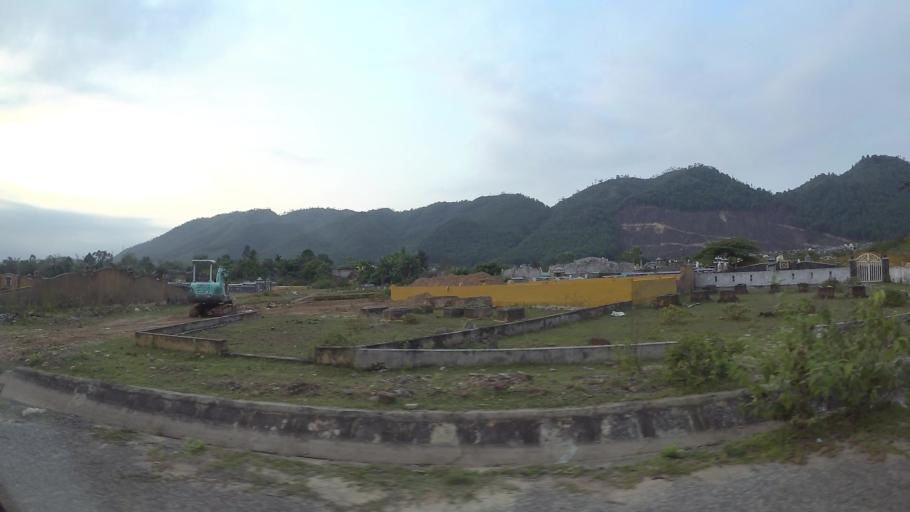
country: VN
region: Da Nang
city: Lien Chieu
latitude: 16.0565
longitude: 108.1255
